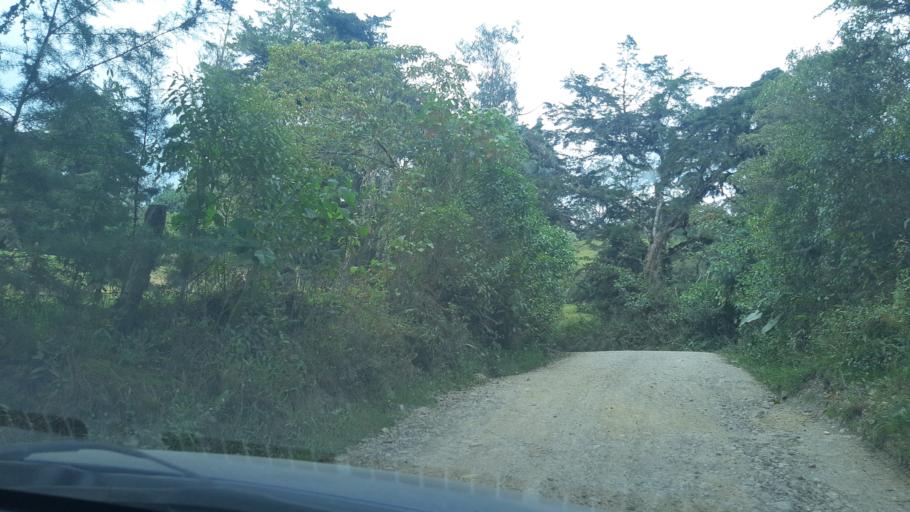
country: CO
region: Boyaca
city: Garagoa
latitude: 5.0864
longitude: -73.3393
